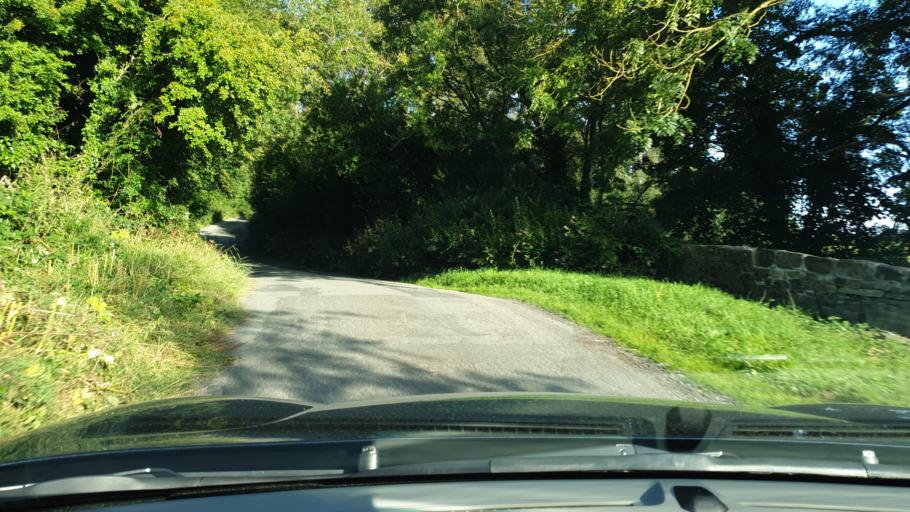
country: IE
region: Leinster
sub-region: An Mhi
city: Stamullin
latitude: 53.6014
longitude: -6.2720
